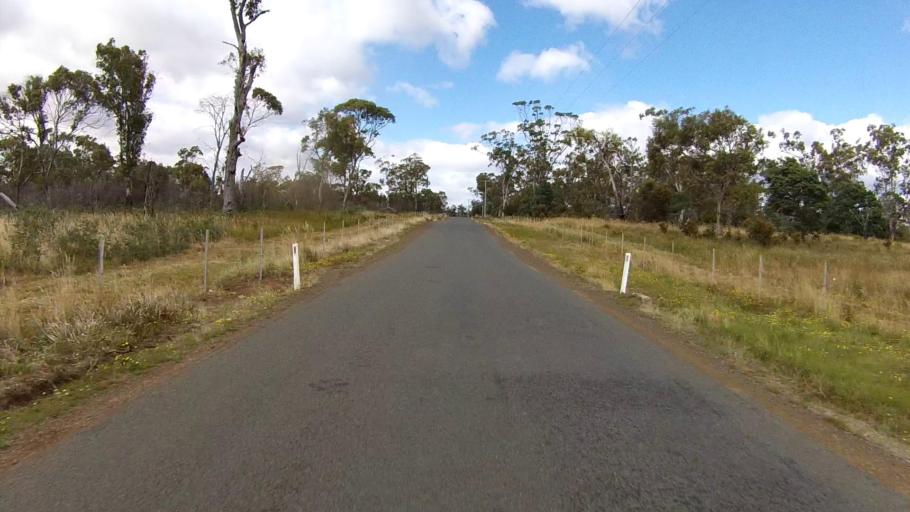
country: AU
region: Tasmania
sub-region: Northern Midlands
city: Evandale
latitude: -41.8146
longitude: 147.4250
